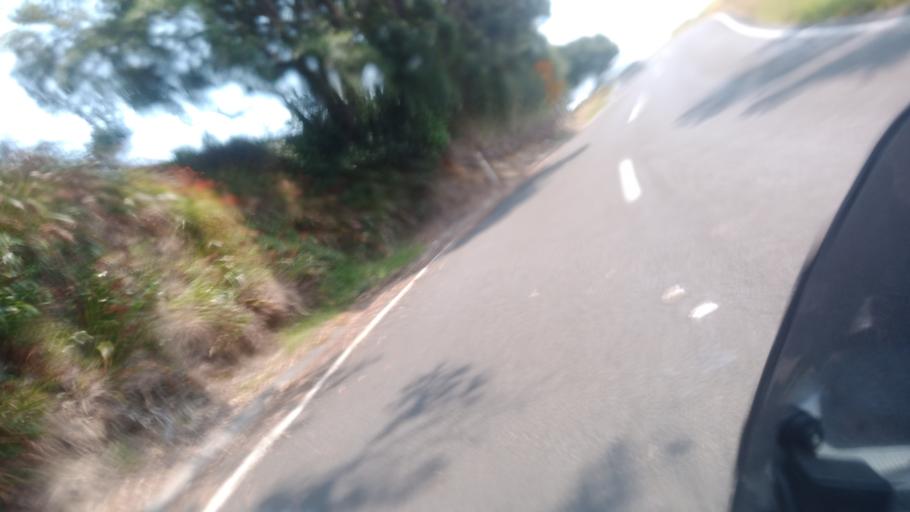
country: NZ
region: Bay of Plenty
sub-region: Opotiki District
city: Opotiki
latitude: -37.5911
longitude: 177.9784
